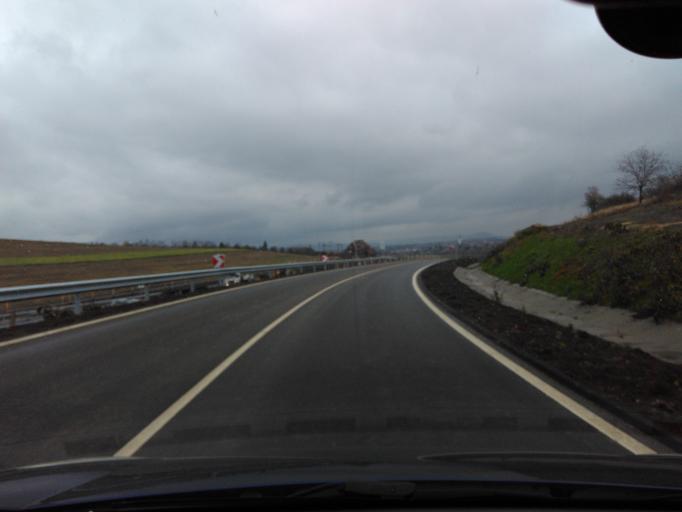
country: HU
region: Nograd
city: Paszto
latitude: 47.9027
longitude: 19.6781
